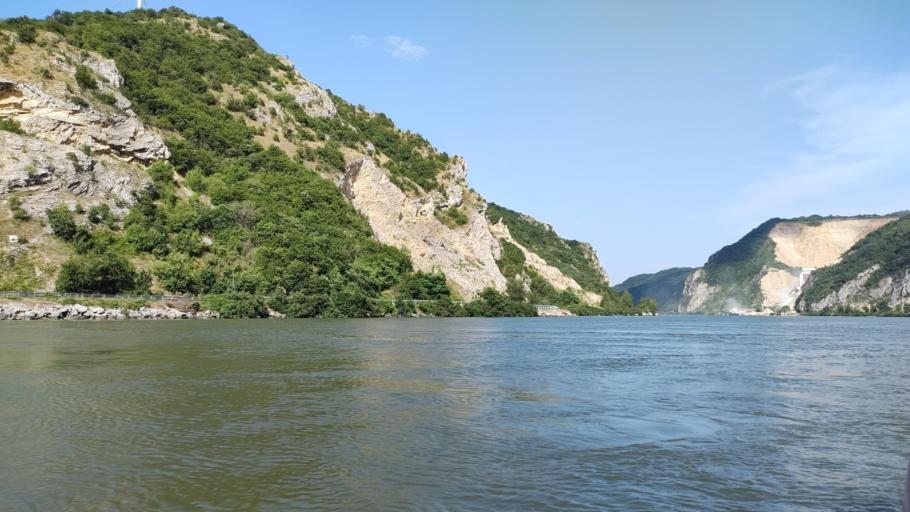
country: RO
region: Caras-Severin
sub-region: Comuna Pescari
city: Coronini
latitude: 44.6556
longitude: 21.7136
